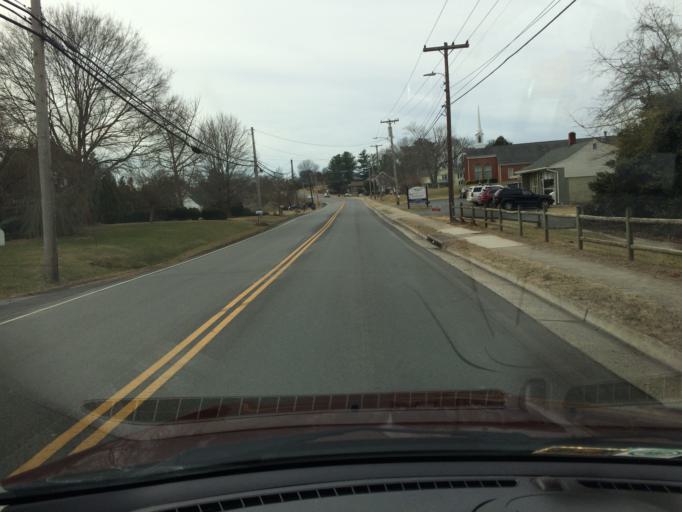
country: US
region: Virginia
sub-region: City of Bedford
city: Bedford
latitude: 37.3461
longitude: -79.5075
